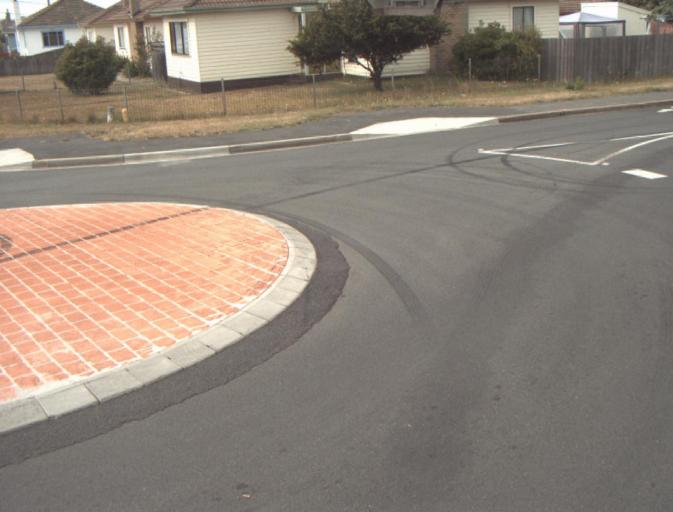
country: AU
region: Tasmania
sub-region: Launceston
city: Mayfield
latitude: -41.3883
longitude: 147.1330
